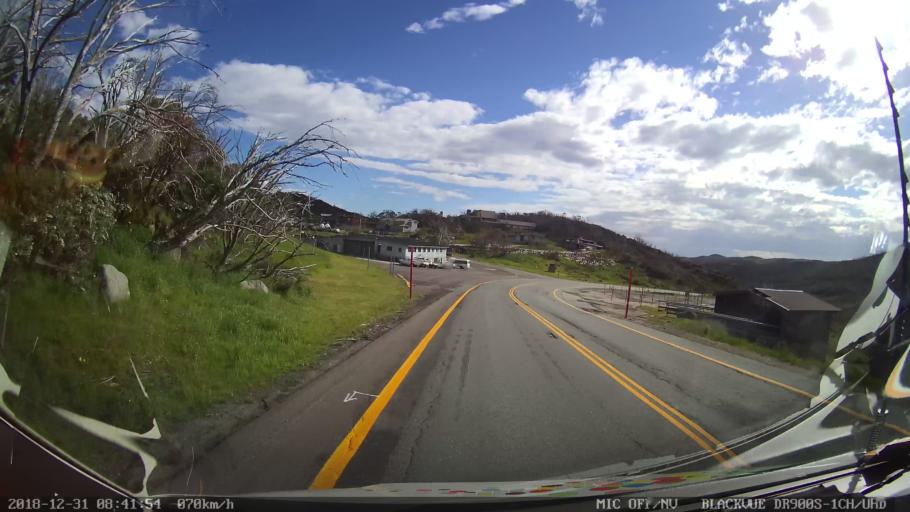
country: AU
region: New South Wales
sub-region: Snowy River
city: Jindabyne
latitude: -36.3951
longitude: 148.4264
